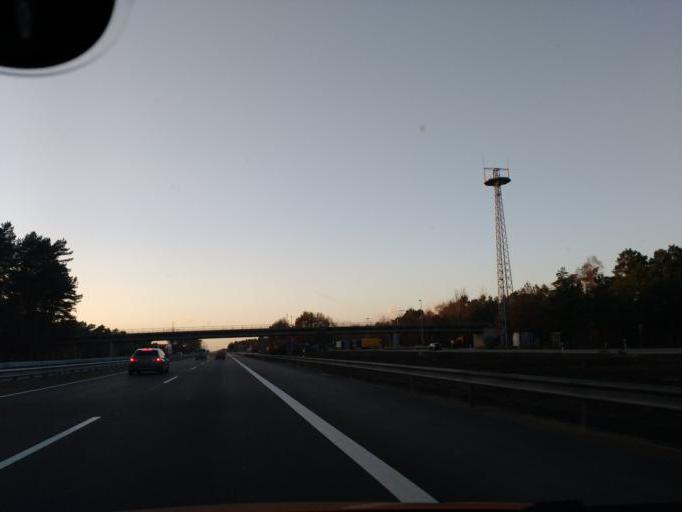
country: DE
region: Schleswig-Holstein
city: Gudow
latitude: 53.5181
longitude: 10.8156
